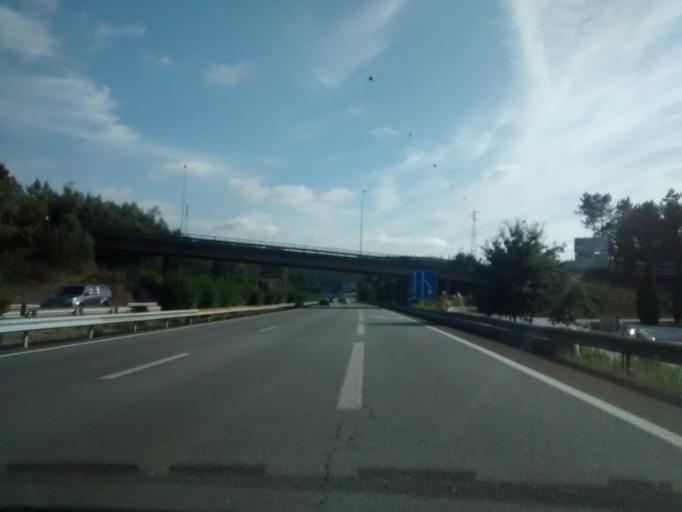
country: PT
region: Porto
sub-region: Santo Tirso
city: Santo Tirso
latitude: 41.3406
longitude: -8.5074
